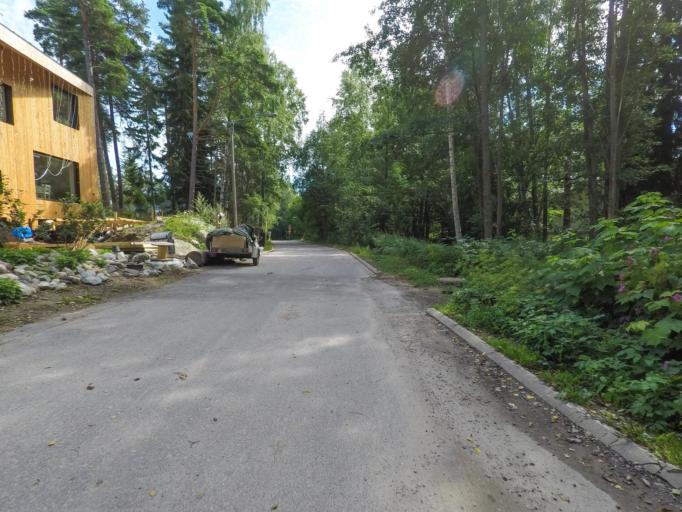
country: FI
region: Uusimaa
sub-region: Helsinki
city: Vantaa
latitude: 60.1655
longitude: 25.0717
